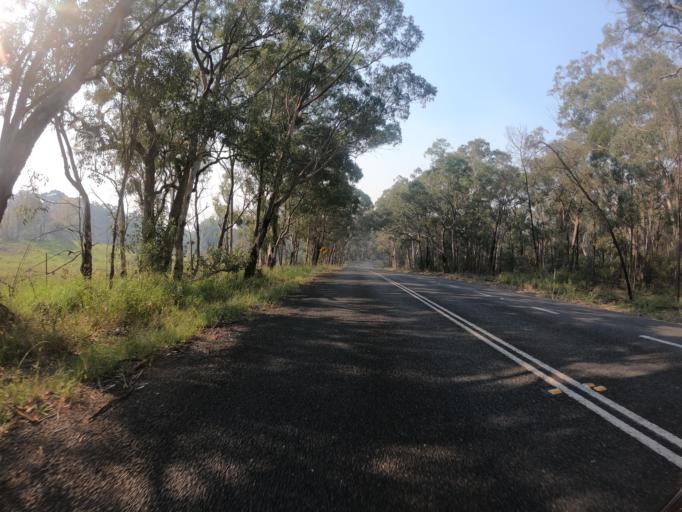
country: AU
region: New South Wales
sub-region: Wollondilly
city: Douglas Park
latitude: -34.2307
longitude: 150.7387
